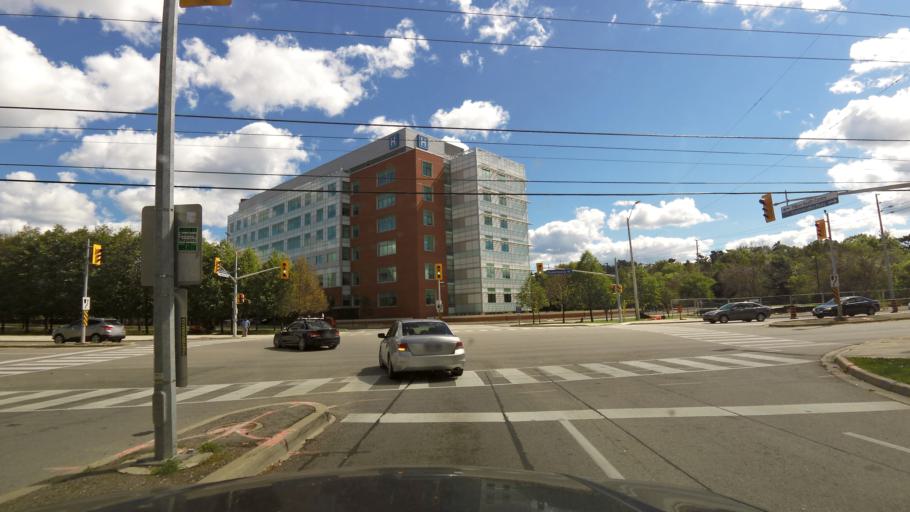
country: CA
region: Ontario
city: Mississauga
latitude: 43.5716
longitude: -79.6109
